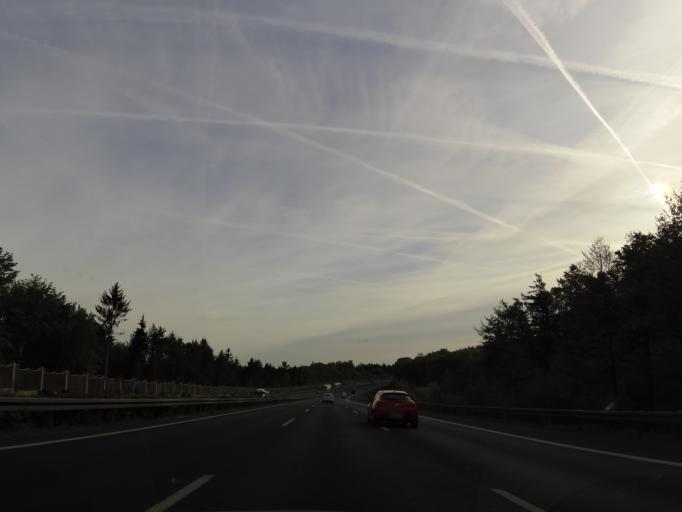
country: DE
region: Lower Saxony
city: Hannoversch Munden
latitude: 51.3902
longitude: 9.6639
